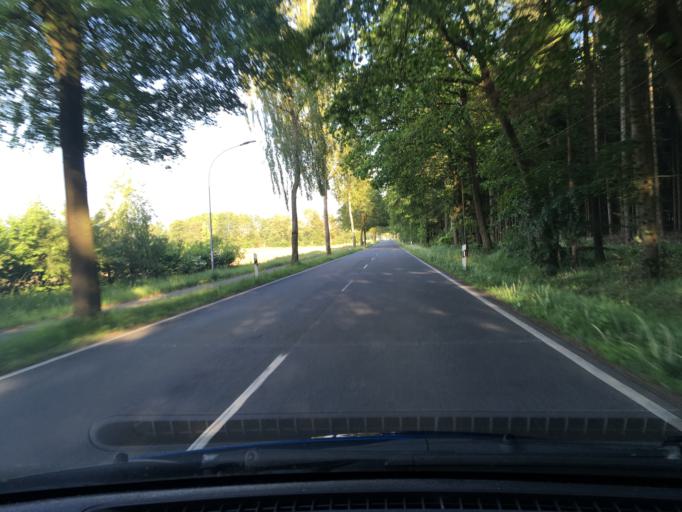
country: DE
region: Lower Saxony
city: Otter
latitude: 53.2503
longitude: 9.7717
